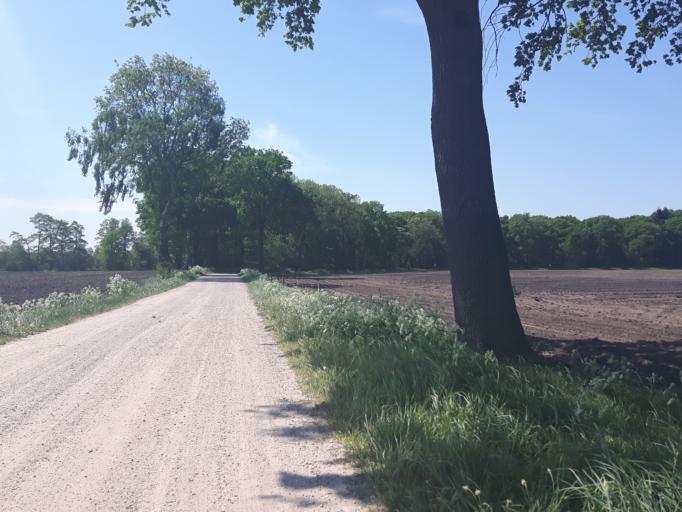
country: NL
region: Overijssel
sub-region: Gemeente Enschede
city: Enschede
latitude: 52.1577
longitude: 6.8833
